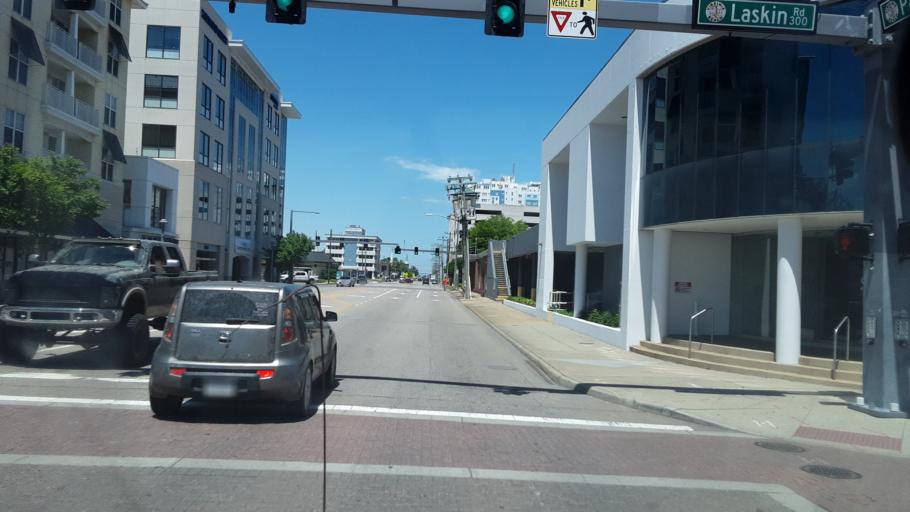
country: US
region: Virginia
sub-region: City of Virginia Beach
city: Virginia Beach
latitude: 36.8591
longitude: -75.9792
